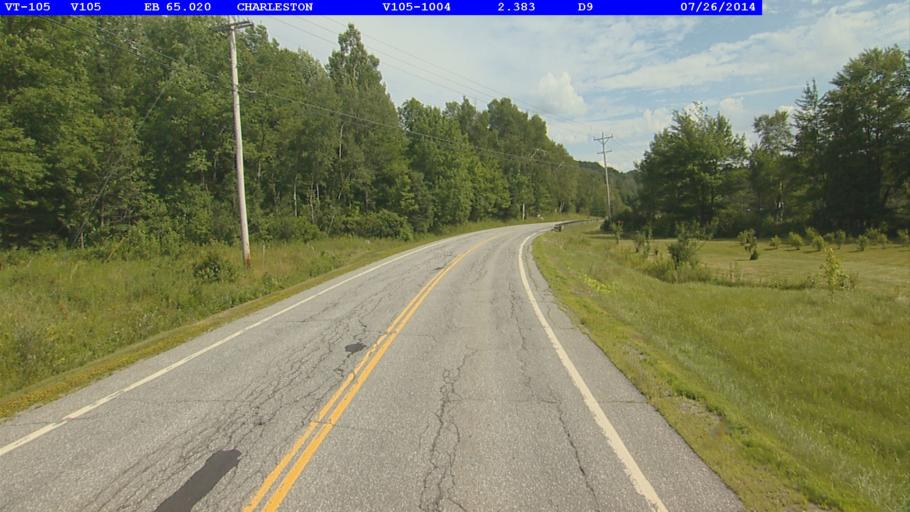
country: US
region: Vermont
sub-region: Orleans County
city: Newport
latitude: 44.8819
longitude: -72.0523
